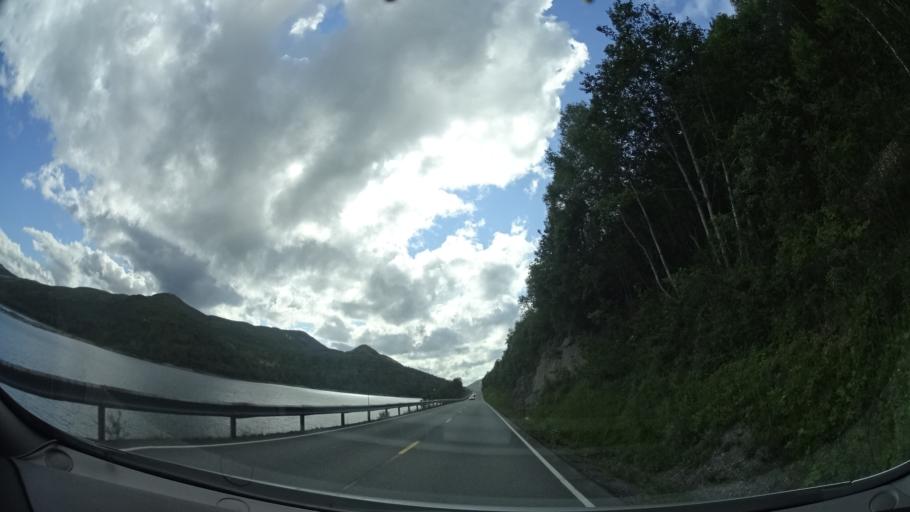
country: NO
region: More og Romsdal
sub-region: Rindal
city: Rindal
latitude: 63.2219
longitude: 9.2764
